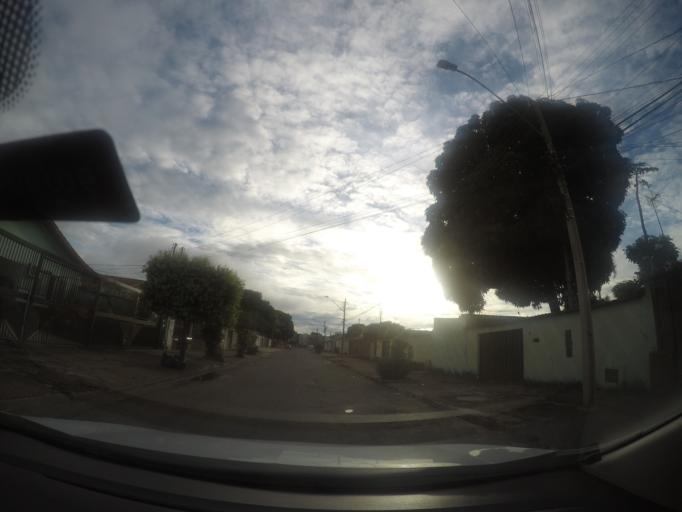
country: BR
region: Goias
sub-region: Goiania
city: Goiania
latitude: -16.6847
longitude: -49.3128
